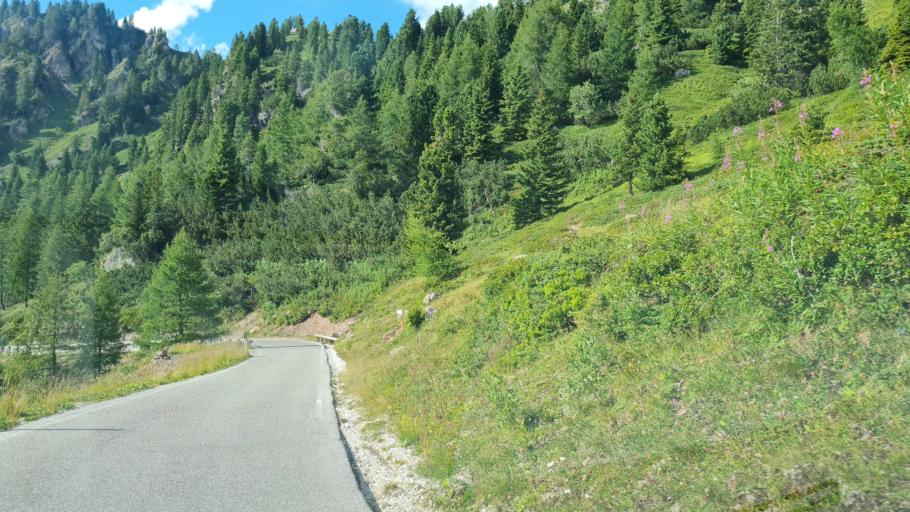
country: IT
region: Trentino-Alto Adige
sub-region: Provincia di Trento
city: Torcegno
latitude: 46.1699
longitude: 11.4430
